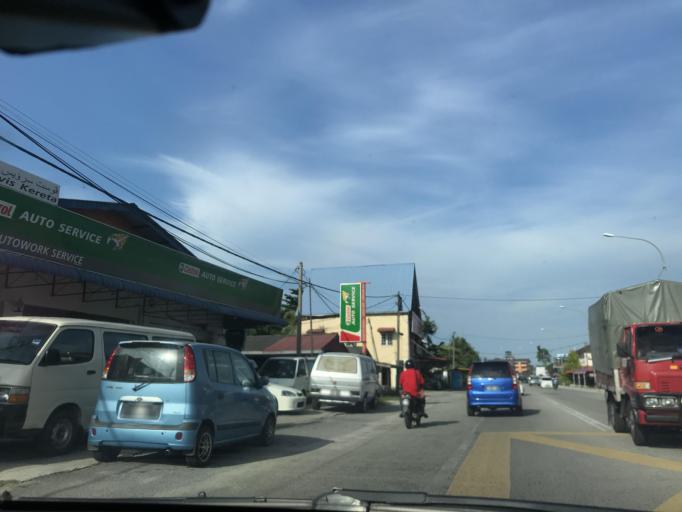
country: MY
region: Kelantan
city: Kota Bharu
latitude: 6.1241
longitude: 102.2743
